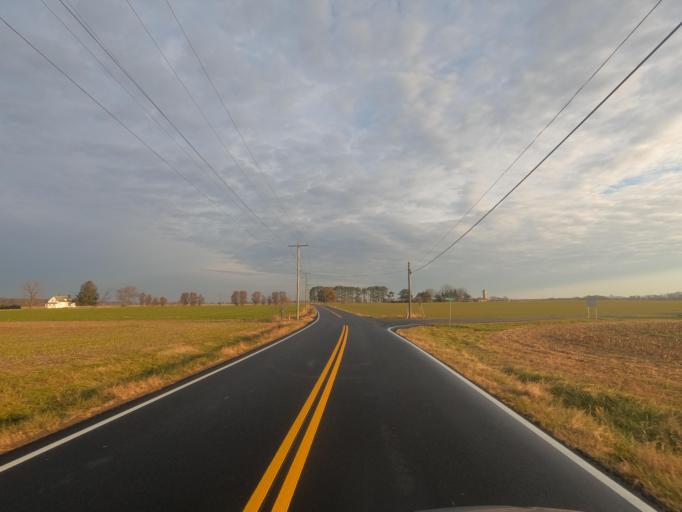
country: US
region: Delaware
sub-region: New Castle County
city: Townsend
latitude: 39.2901
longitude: -75.8326
